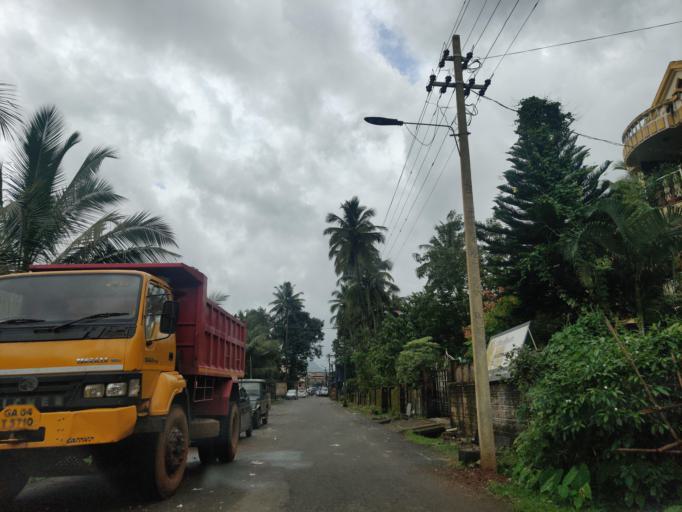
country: IN
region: Goa
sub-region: North Goa
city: Valpoy
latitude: 15.5294
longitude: 74.1376
